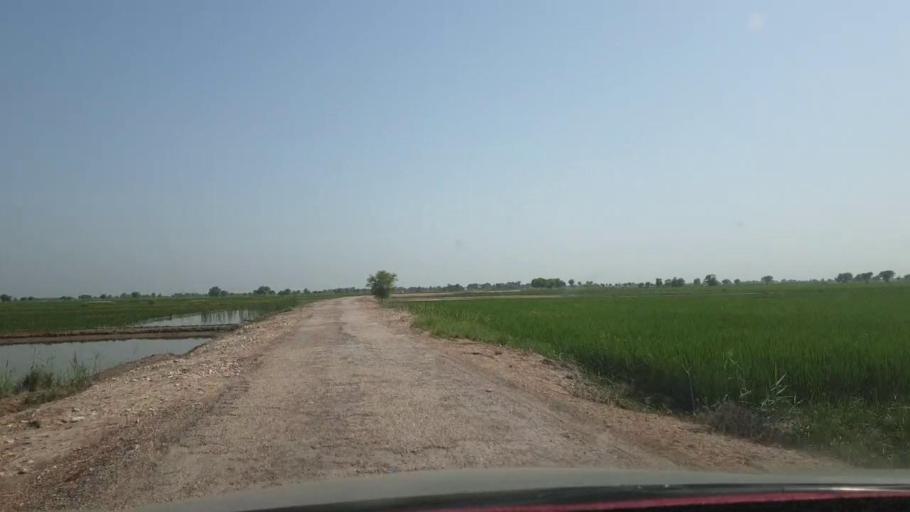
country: PK
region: Sindh
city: Nasirabad
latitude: 27.3687
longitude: 67.8530
